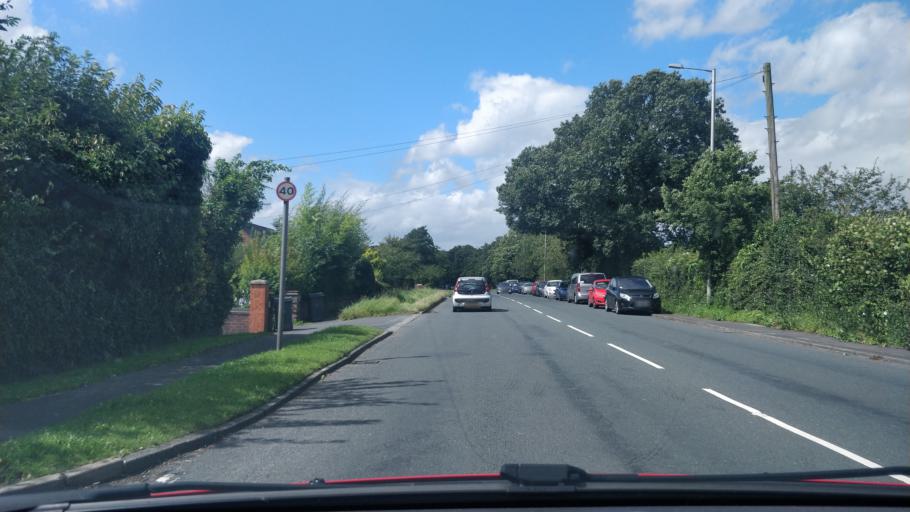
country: GB
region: England
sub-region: Lancashire
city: Appley Bridge
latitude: 53.5925
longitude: -2.7274
